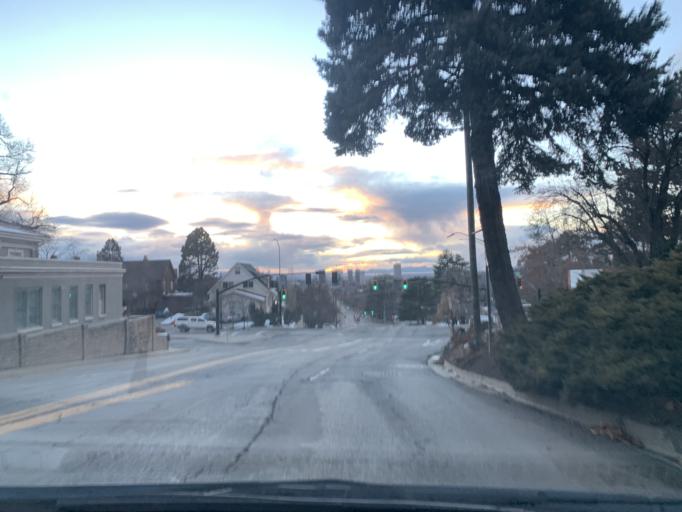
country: US
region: Utah
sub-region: Salt Lake County
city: Salt Lake City
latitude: 40.7671
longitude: -111.8515
